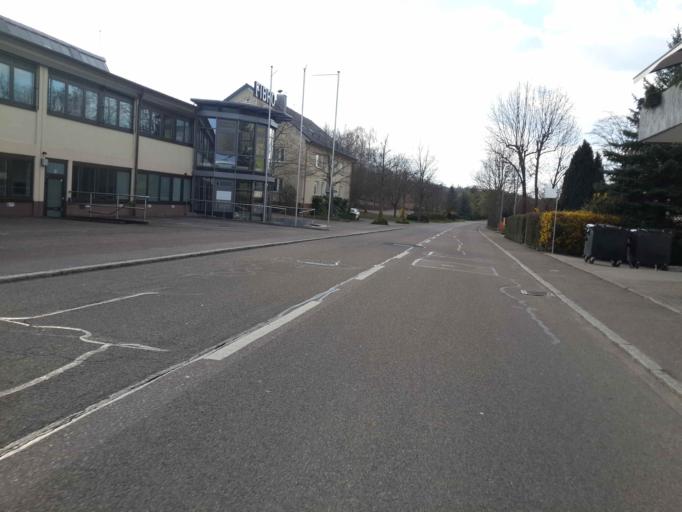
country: DE
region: Baden-Wuerttemberg
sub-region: Regierungsbezirk Stuttgart
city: Weinsberg
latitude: 49.1534
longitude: 9.2744
